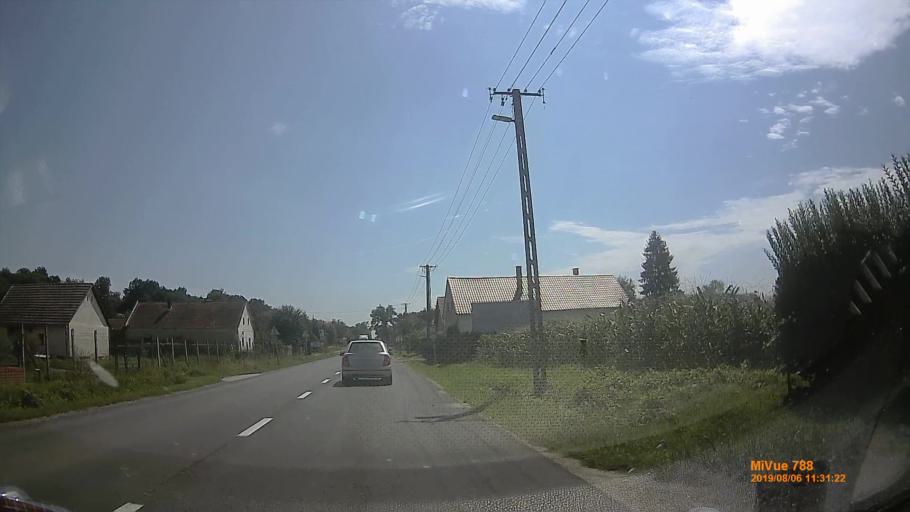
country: AT
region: Burgenland
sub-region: Politischer Bezirk Gussing
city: Inzenhof
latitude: 46.9764
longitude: 16.3707
